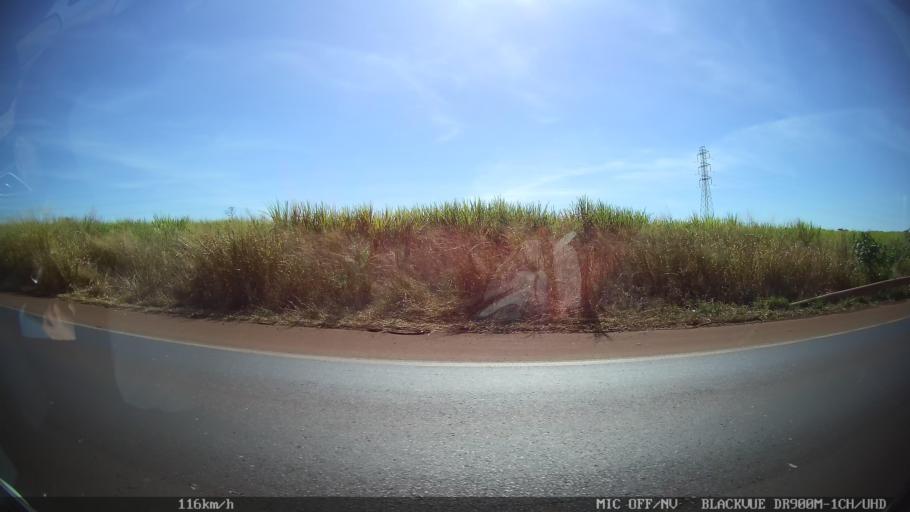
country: BR
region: Sao Paulo
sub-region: Barretos
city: Barretos
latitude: -20.5040
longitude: -48.5471
